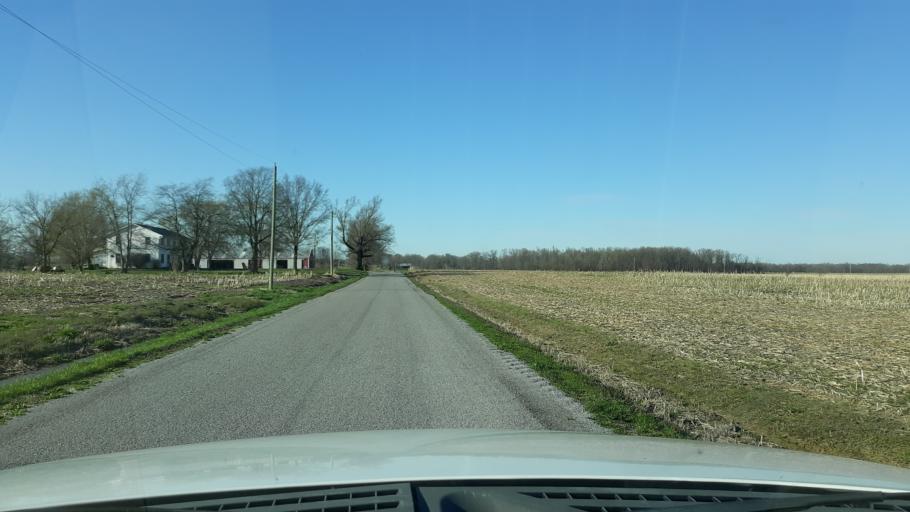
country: US
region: Illinois
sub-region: Saline County
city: Harrisburg
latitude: 37.7687
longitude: -88.5864
